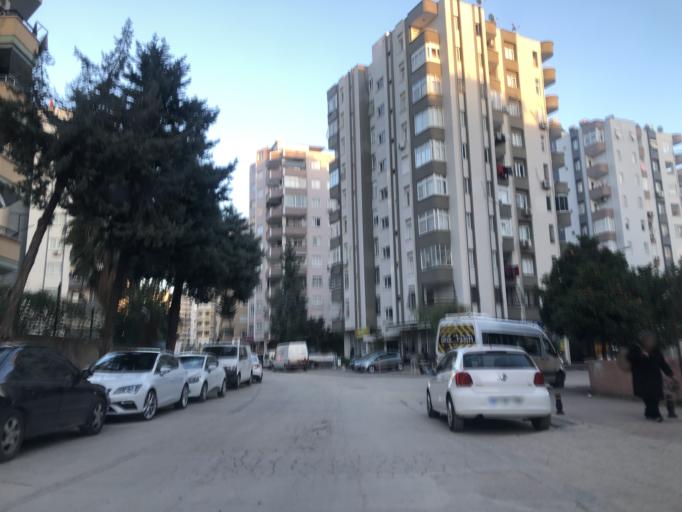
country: TR
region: Adana
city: Adana
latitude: 37.0456
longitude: 35.2974
